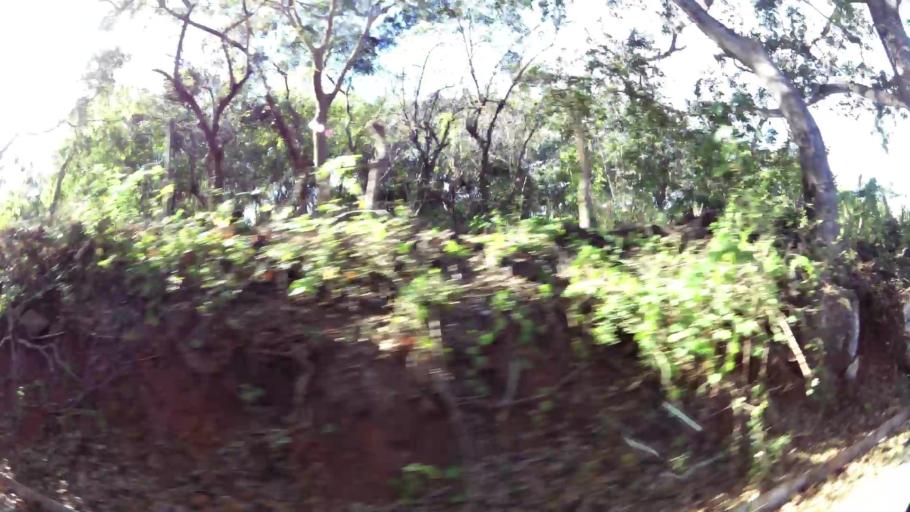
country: SV
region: Cuscatlan
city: Suchitoto
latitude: 13.9422
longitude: -89.0167
